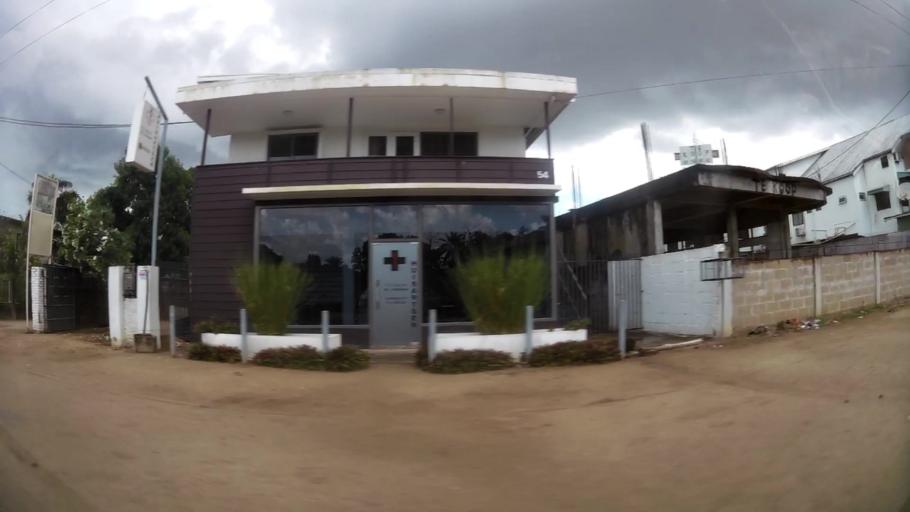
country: SR
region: Paramaribo
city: Paramaribo
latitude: 5.8356
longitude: -55.1697
